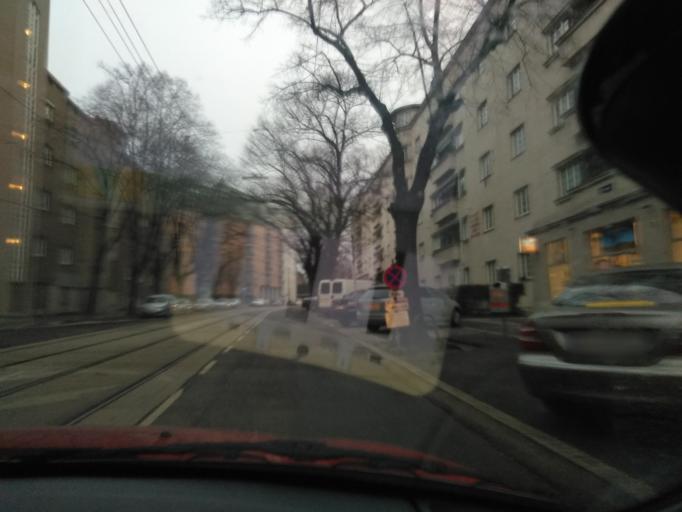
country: AT
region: Vienna
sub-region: Wien Stadt
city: Vienna
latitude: 48.2268
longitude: 16.3298
